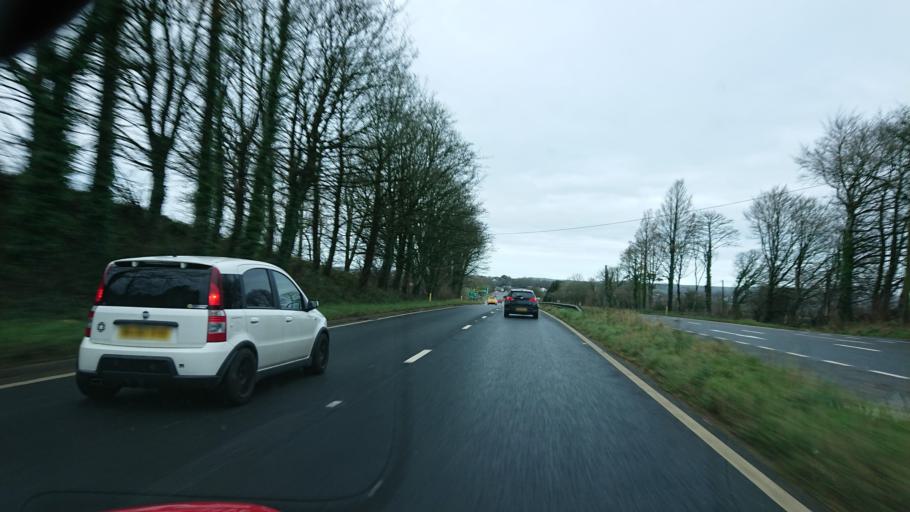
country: GB
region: England
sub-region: Cornwall
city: Liskeard
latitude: 50.4428
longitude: -4.4452
